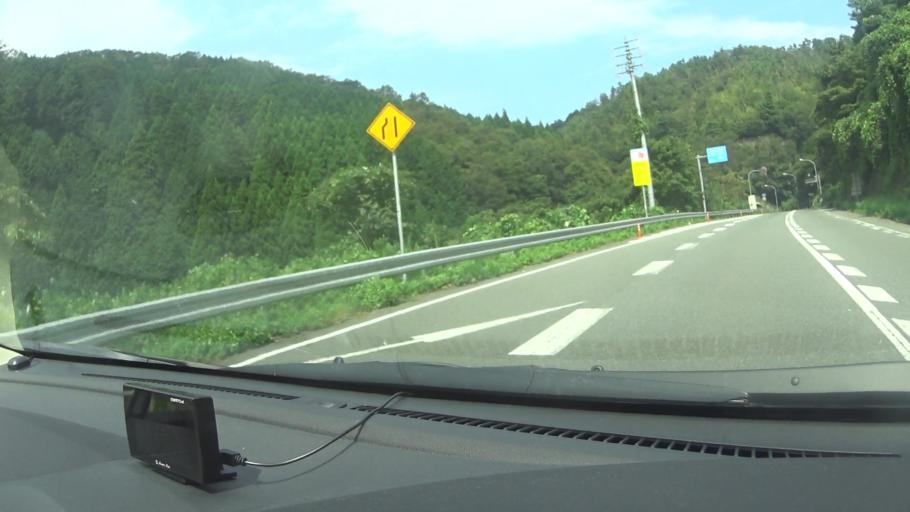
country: JP
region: Kyoto
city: Ayabe
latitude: 35.2672
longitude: 135.2711
